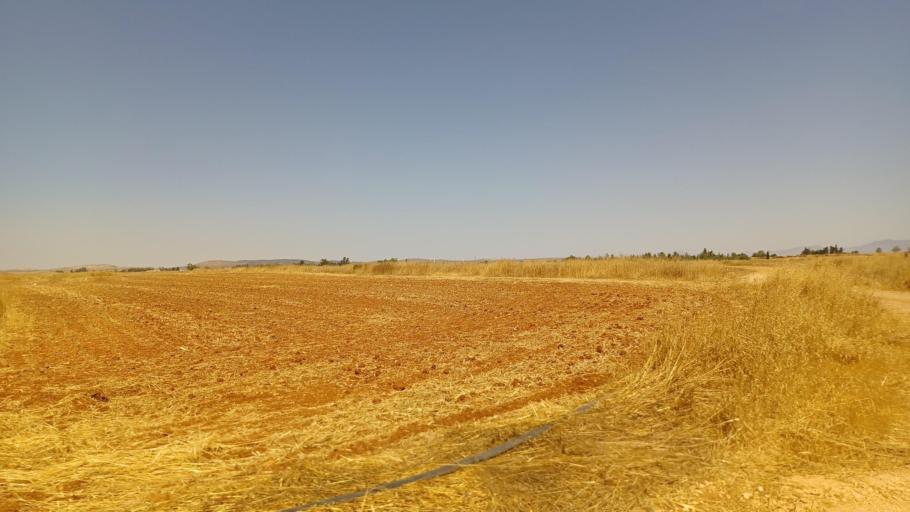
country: CY
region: Larnaka
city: Xylotymbou
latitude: 35.0305
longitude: 33.7293
